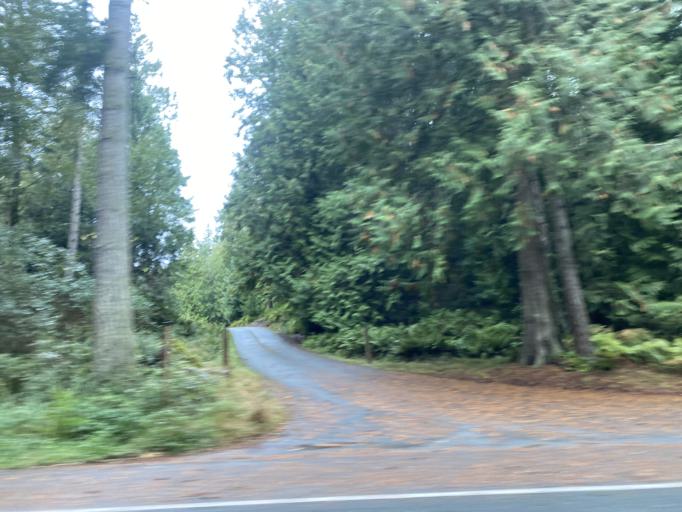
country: US
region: Washington
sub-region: Island County
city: Langley
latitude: 48.0236
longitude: -122.4088
